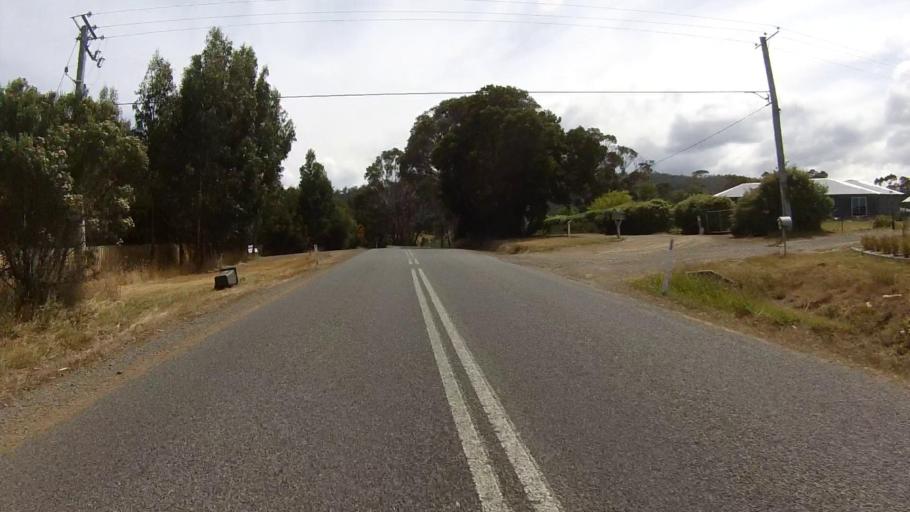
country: AU
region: Tasmania
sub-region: Huon Valley
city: Cygnet
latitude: -43.1891
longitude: 147.1004
